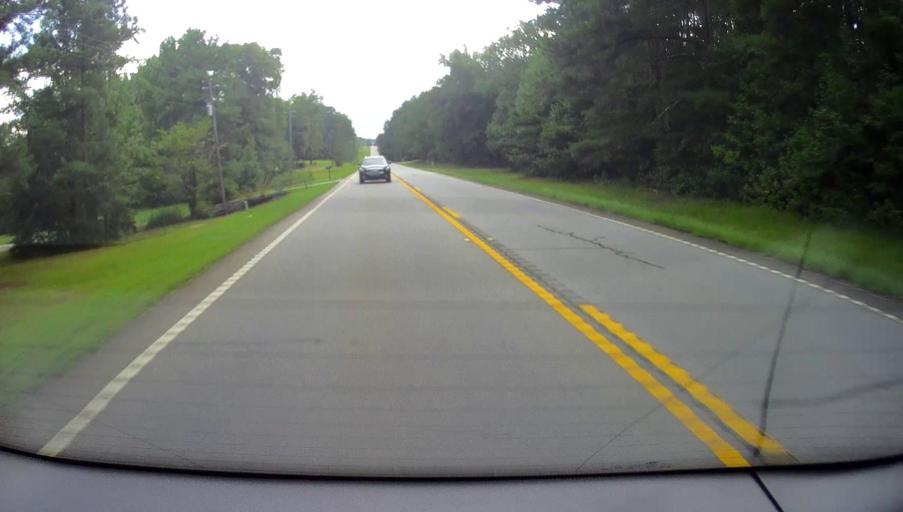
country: US
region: Georgia
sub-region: Coweta County
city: Senoia
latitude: 33.1502
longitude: -84.5867
